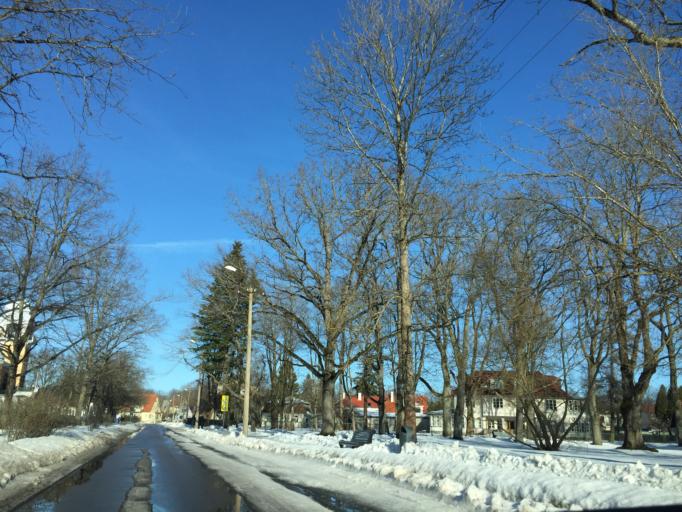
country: EE
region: Paernumaa
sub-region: Paernu linn
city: Parnu
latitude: 58.3793
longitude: 24.4927
